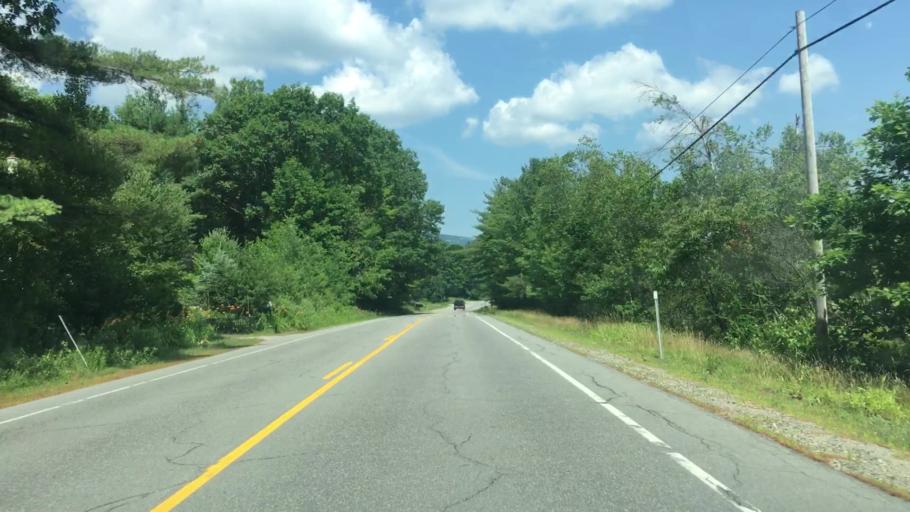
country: US
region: New Hampshire
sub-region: Sullivan County
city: Grantham
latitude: 43.4463
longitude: -72.1601
